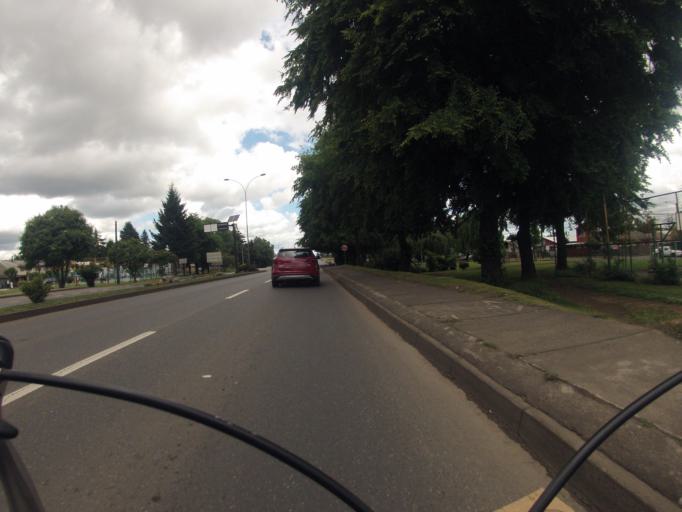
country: CL
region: Araucania
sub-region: Provincia de Cautin
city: Temuco
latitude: -38.7508
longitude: -72.6092
